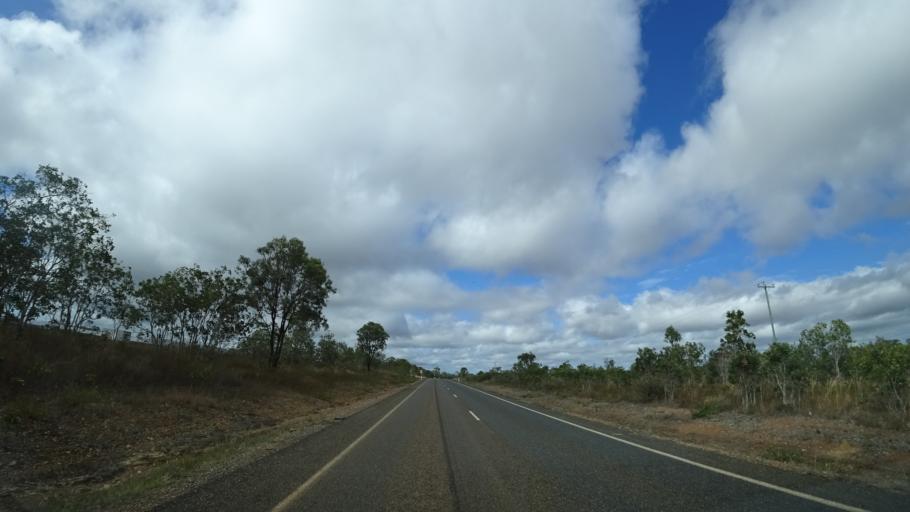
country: AU
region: Queensland
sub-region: Cook
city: Cooktown
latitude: -15.8687
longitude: 144.8597
